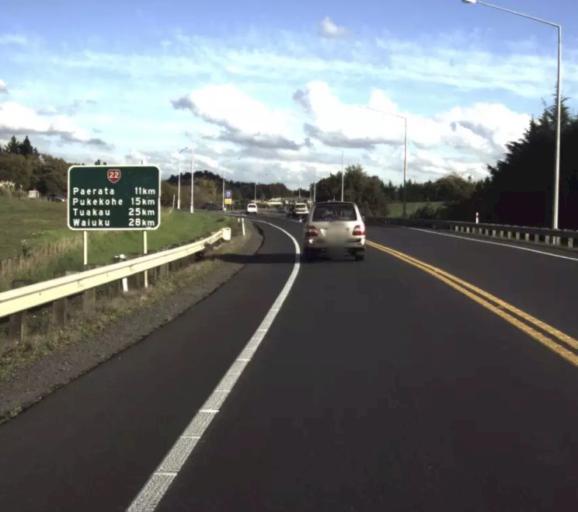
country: NZ
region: Auckland
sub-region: Auckland
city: Papakura
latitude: -37.1108
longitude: 174.9427
